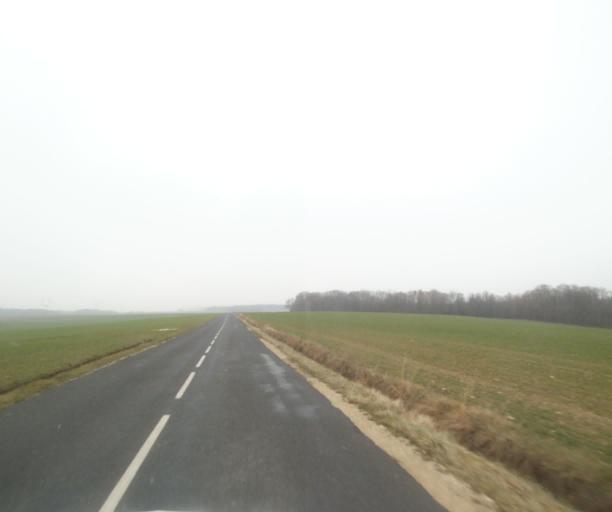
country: FR
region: Champagne-Ardenne
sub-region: Departement de la Haute-Marne
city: Bienville
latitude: 48.5210
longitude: 5.0667
